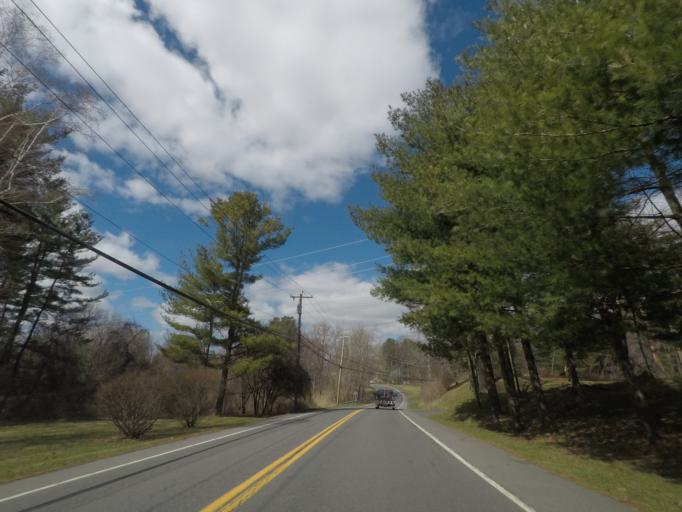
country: US
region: New York
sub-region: Albany County
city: Delmar
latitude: 42.5911
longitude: -73.8337
